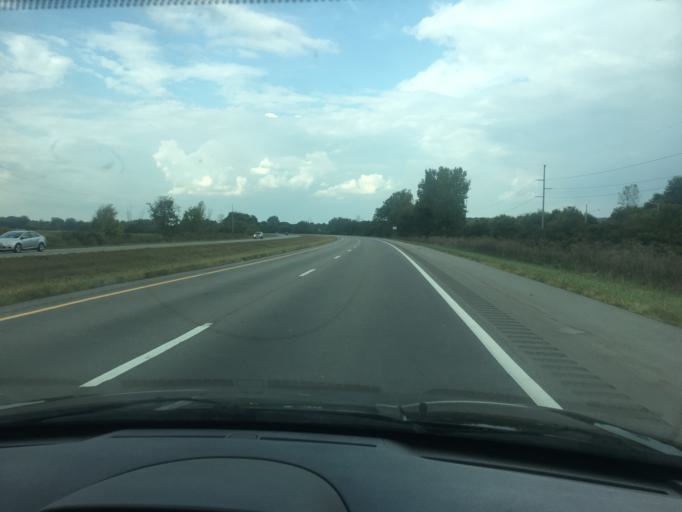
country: US
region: Ohio
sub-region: Clark County
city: Springfield
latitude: 39.9650
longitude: -83.8204
